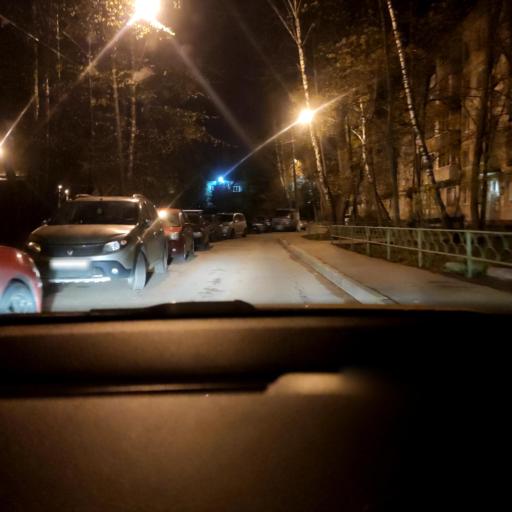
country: RU
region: Moskovskaya
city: Odintsovo
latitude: 55.6726
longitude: 37.2649
